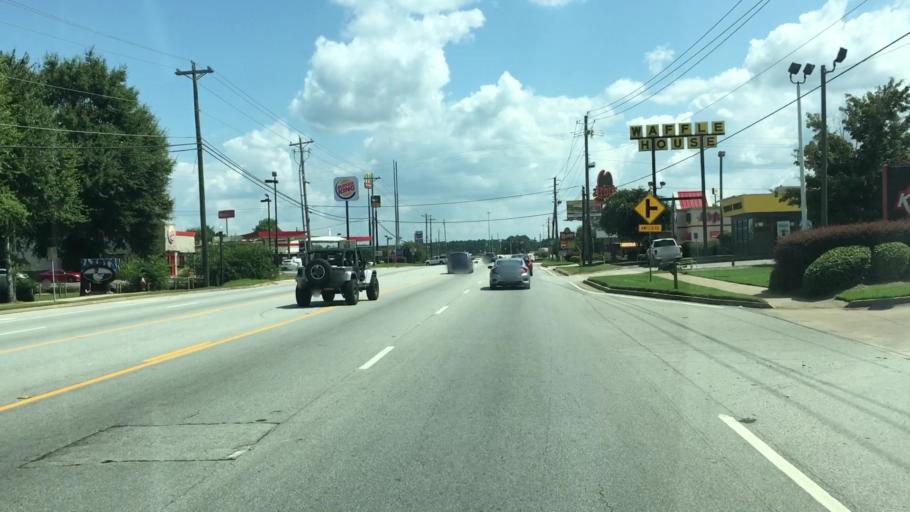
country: US
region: Georgia
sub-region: Morgan County
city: Madison
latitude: 33.5601
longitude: -83.4773
